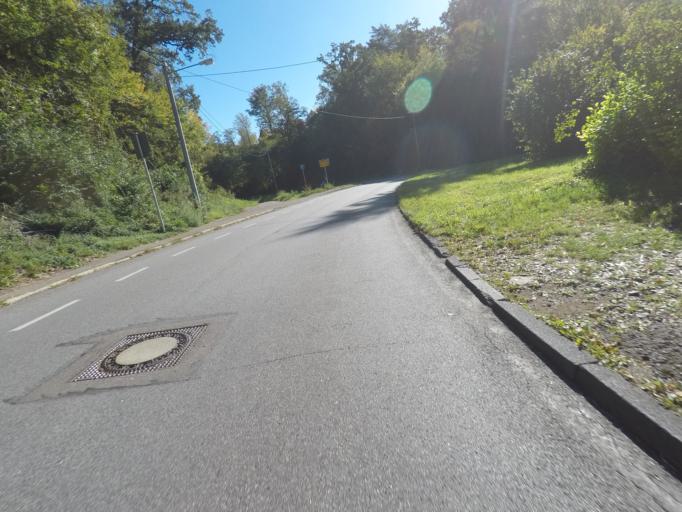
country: DE
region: Baden-Wuerttemberg
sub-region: Regierungsbezirk Stuttgart
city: Stuttgart
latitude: 48.7451
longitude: 9.1300
